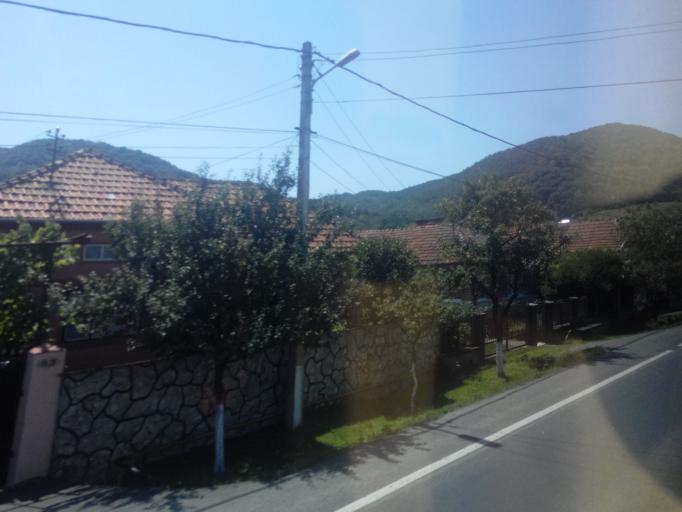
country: RO
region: Hunedoara
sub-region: Comuna Branisca
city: Branisca
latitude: 45.9159
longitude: 22.7308
